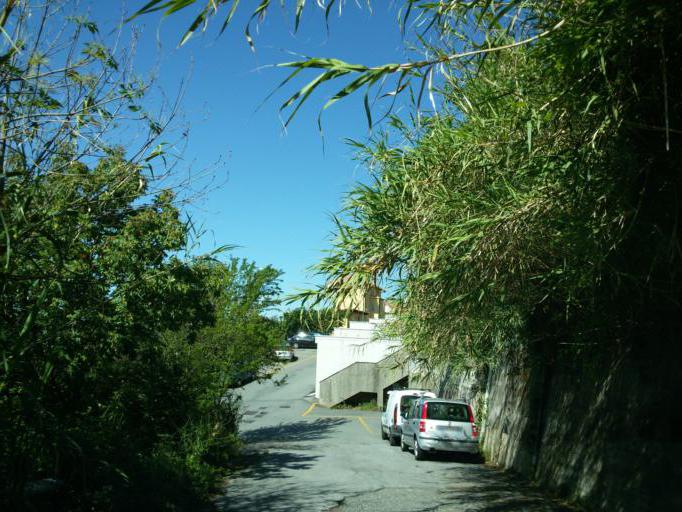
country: IT
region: Liguria
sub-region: Provincia di Genova
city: Piccarello
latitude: 44.4428
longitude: 8.9807
